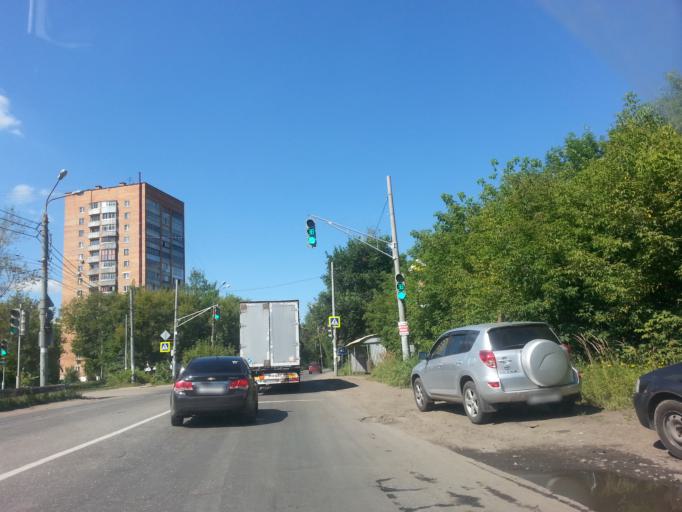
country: RU
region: Nizjnij Novgorod
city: Gorbatovka
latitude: 56.3351
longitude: 43.8491
